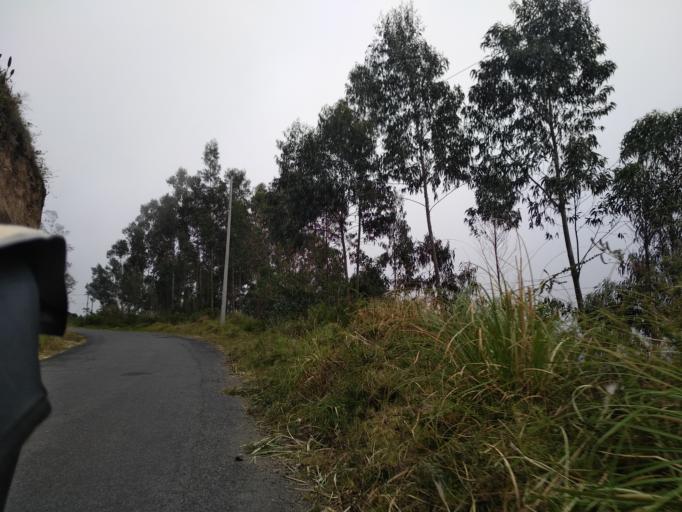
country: EC
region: Cotopaxi
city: Saquisili
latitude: -0.6895
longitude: -78.8280
